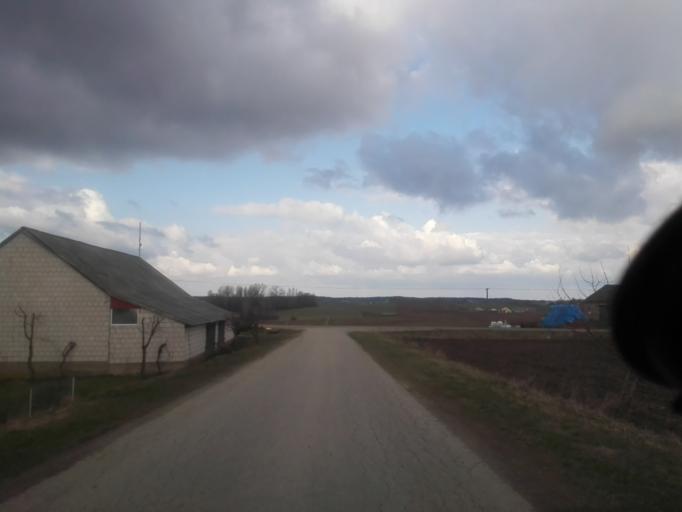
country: PL
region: Podlasie
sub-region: Suwalki
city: Suwalki
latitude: 54.2552
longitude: 22.9615
